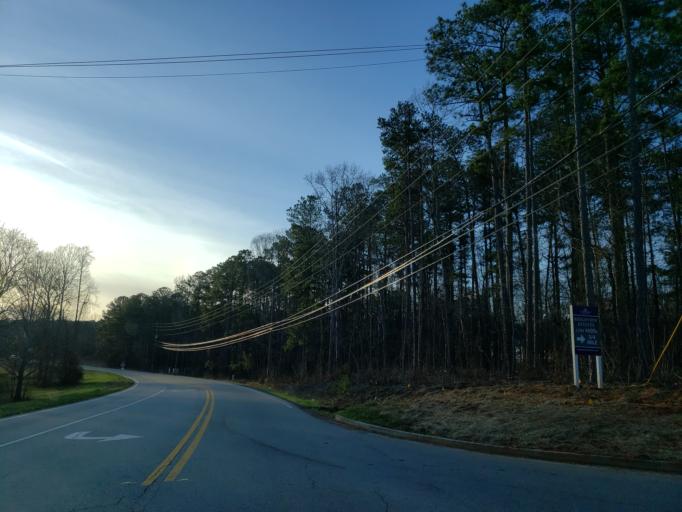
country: US
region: Georgia
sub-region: Cobb County
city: Acworth
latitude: 33.9794
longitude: -84.7352
